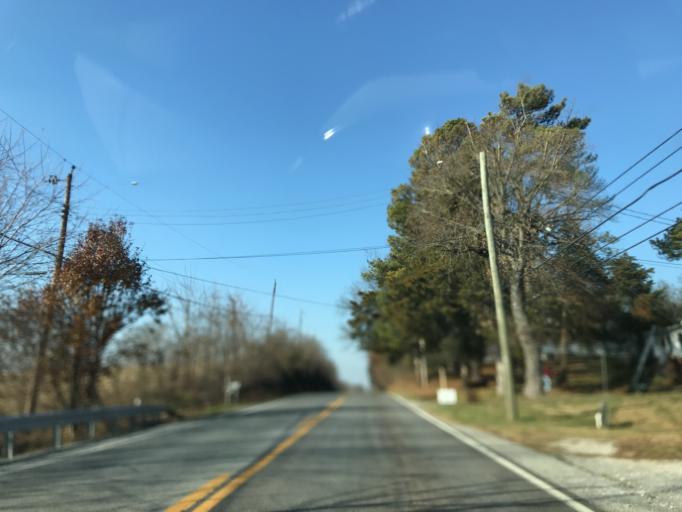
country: US
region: Maryland
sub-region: Carroll County
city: Taneytown
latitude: 39.6378
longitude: -77.1329
